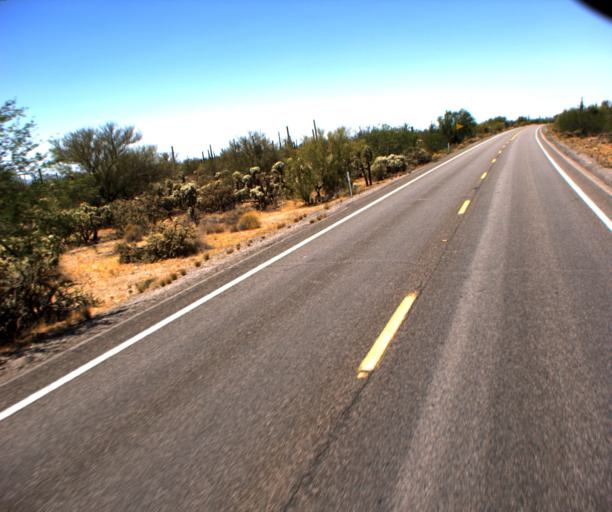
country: US
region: Arizona
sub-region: Pima County
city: Marana
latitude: 32.7672
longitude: -111.1547
